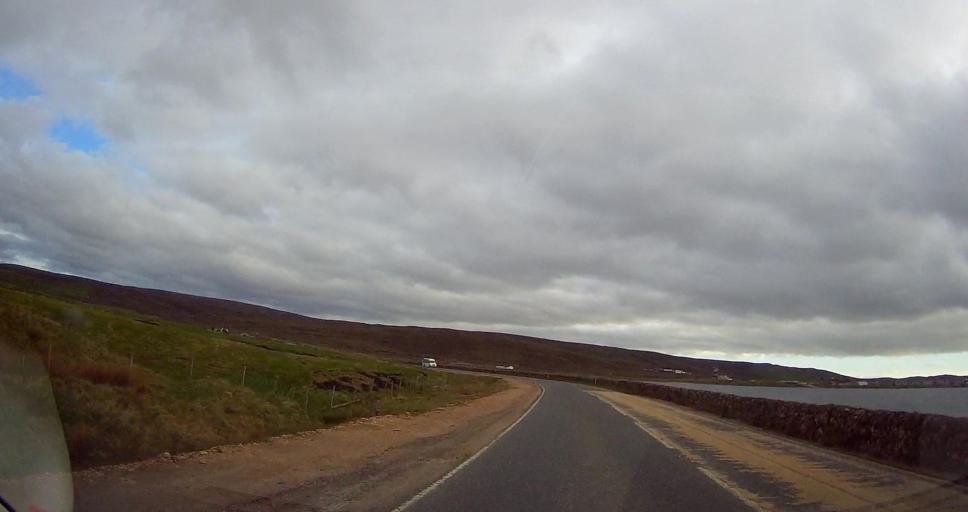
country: GB
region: Scotland
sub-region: Shetland Islands
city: Lerwick
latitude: 60.4486
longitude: -1.2587
